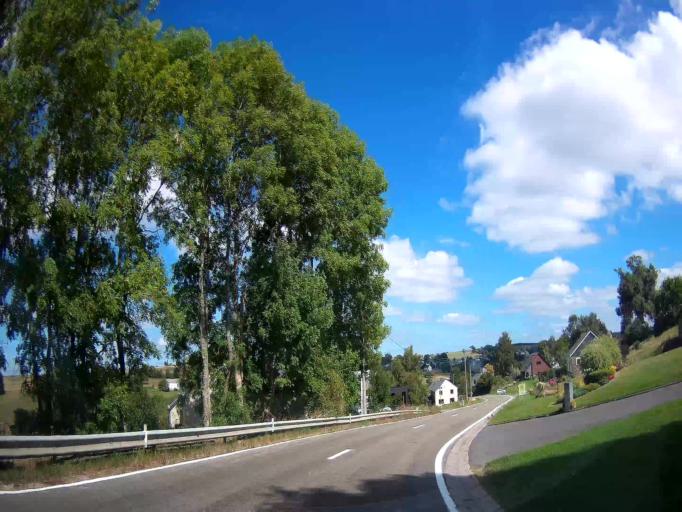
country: BE
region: Wallonia
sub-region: Province du Luxembourg
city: Bertogne
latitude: 50.0465
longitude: 5.6863
